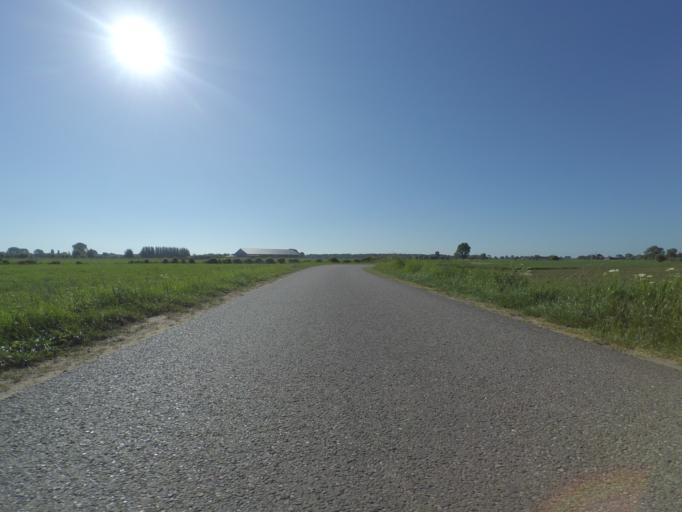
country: NL
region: Gelderland
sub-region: Gemeente Voorst
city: Wilp
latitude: 52.2162
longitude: 6.1731
